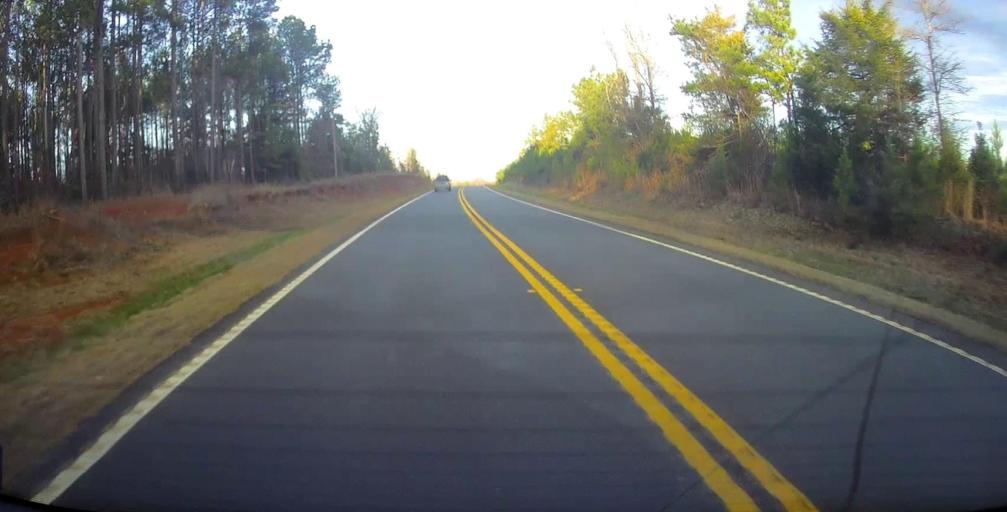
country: US
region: Georgia
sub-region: Talbot County
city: Sardis
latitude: 32.7146
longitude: -84.6839
